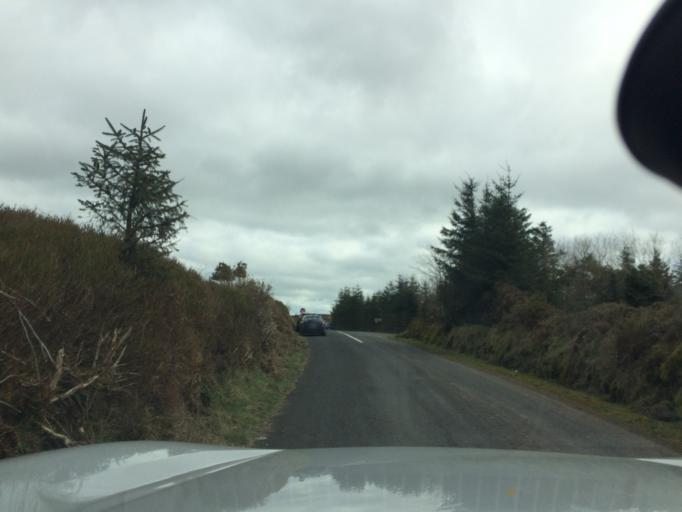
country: IE
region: Munster
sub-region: South Tipperary
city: Cluain Meala
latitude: 52.3342
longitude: -7.6170
